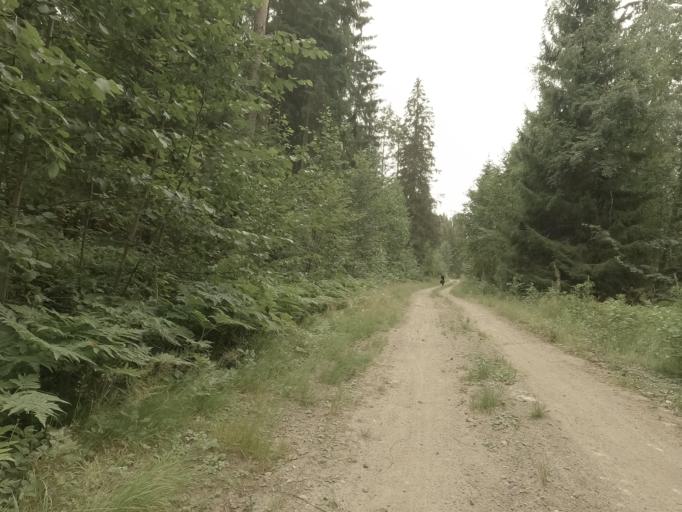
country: RU
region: Leningrad
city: Kamennogorsk
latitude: 61.0696
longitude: 29.1660
